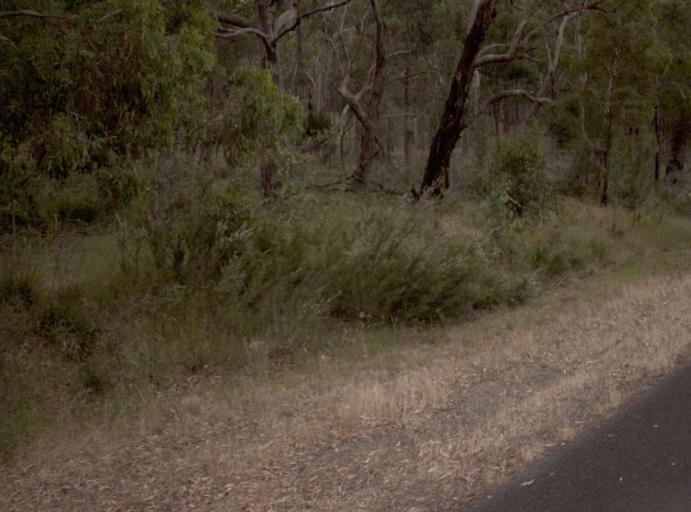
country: AU
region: Victoria
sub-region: Wellington
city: Sale
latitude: -38.4578
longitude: 146.9365
